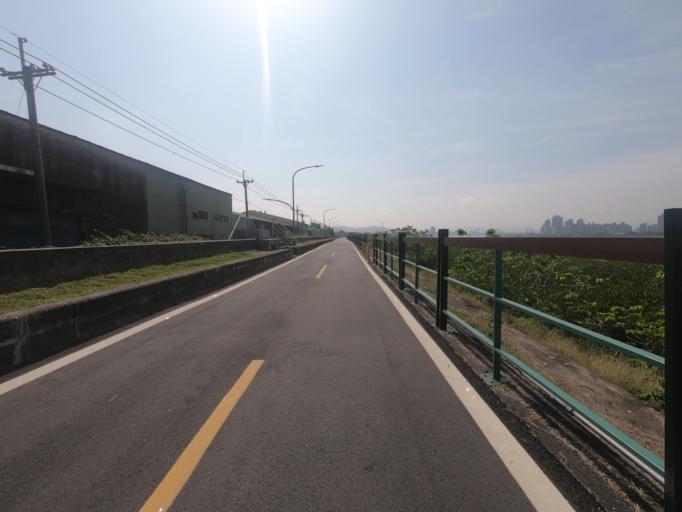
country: TW
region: Taipei
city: Taipei
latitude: 25.1046
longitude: 121.4782
